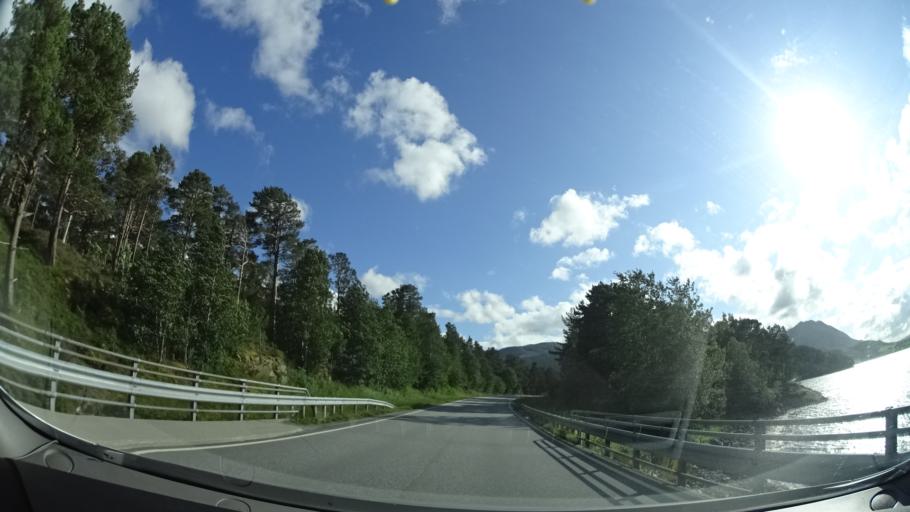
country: NO
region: More og Romsdal
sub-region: Aure
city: Aure
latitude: 63.1412
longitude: 8.5327
